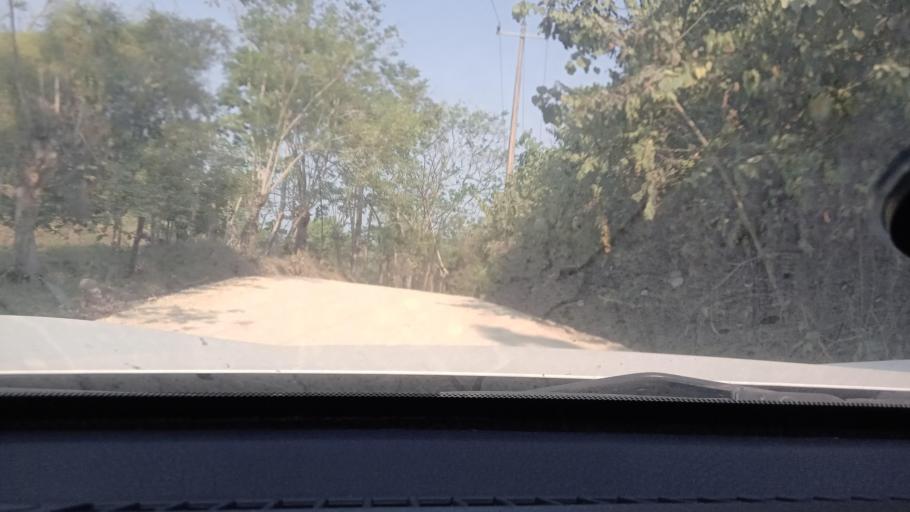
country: MX
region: Tabasco
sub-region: Huimanguillo
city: Francisco Rueda
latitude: 17.6566
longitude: -93.8699
